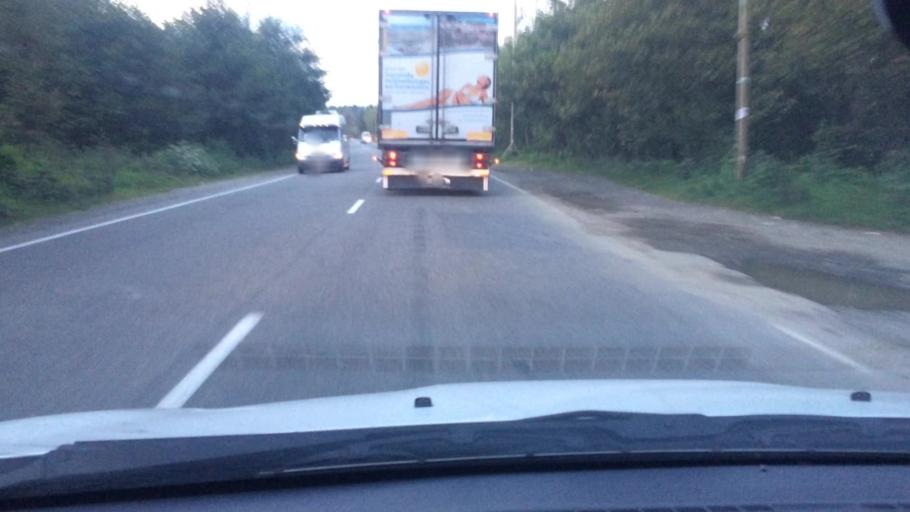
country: GE
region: Guria
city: Urek'i
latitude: 41.9796
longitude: 41.7826
